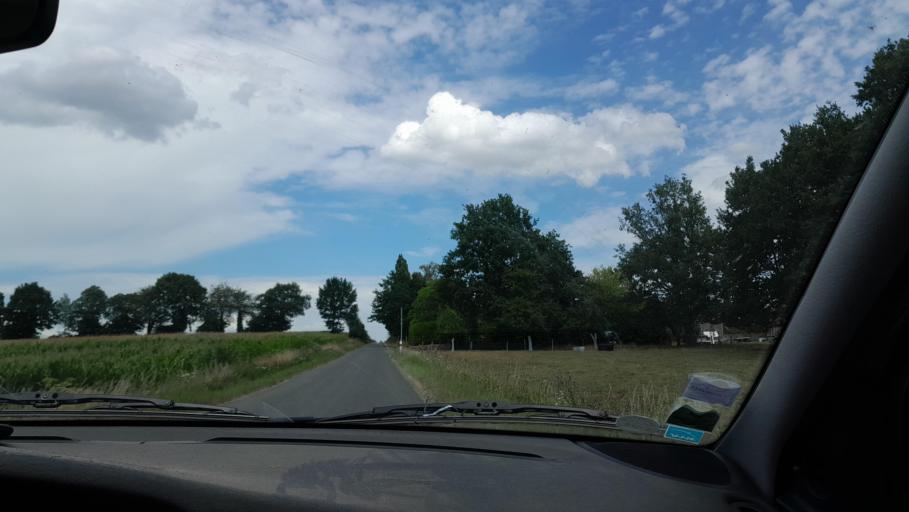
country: FR
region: Pays de la Loire
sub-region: Departement de la Mayenne
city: Juvigne
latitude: 48.1762
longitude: -1.0382
